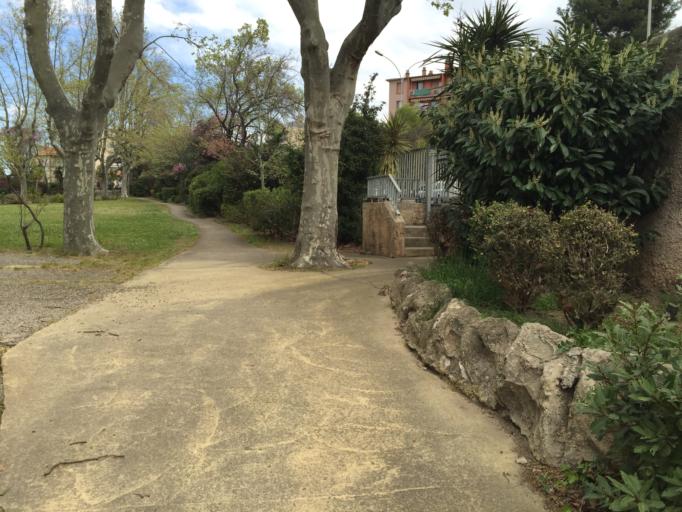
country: FR
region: Provence-Alpes-Cote d'Azur
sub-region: Departement des Bouches-du-Rhone
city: Marseille 09
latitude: 43.2479
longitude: 5.3970
